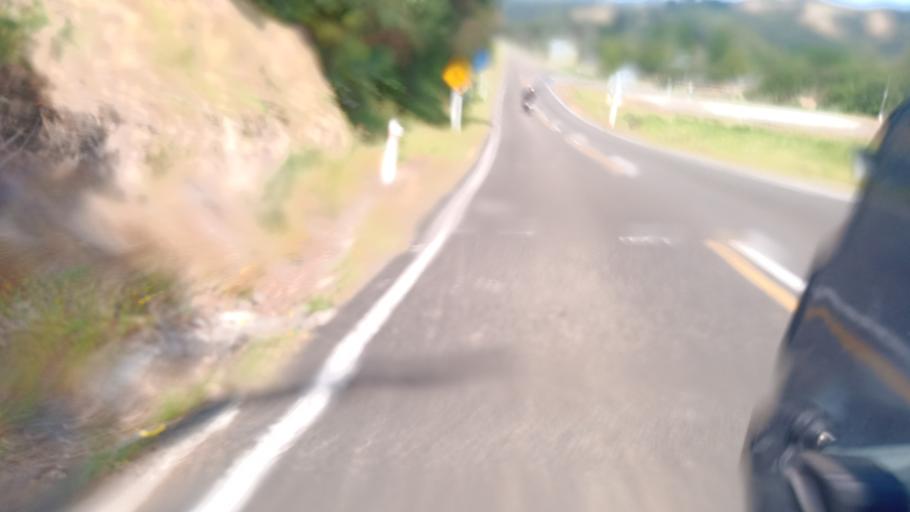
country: NZ
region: Bay of Plenty
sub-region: Opotiki District
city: Opotiki
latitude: -37.5930
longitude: 178.2934
